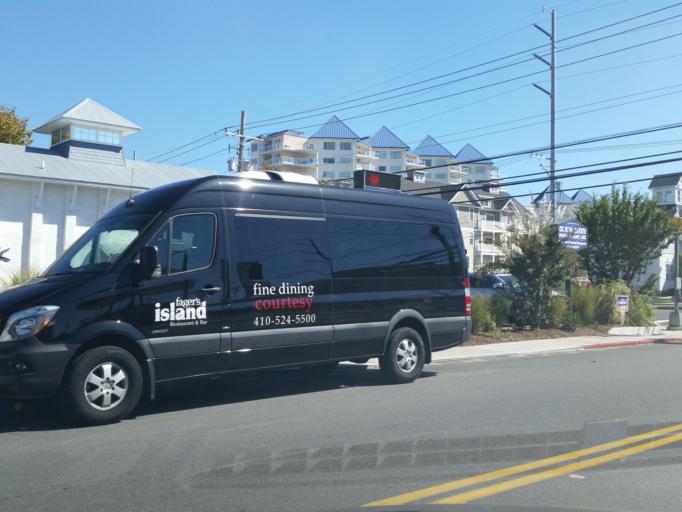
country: US
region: Maryland
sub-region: Worcester County
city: Ocean City
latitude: 38.3827
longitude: -75.0677
